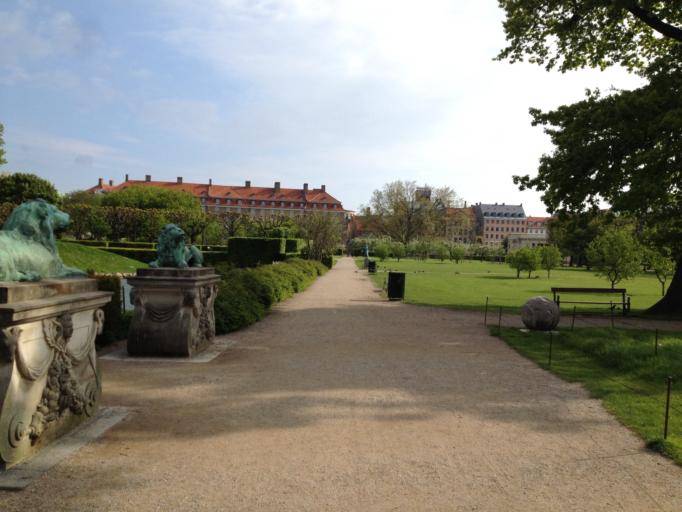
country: DK
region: Capital Region
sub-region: Kobenhavn
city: Copenhagen
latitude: 55.6853
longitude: 12.5781
